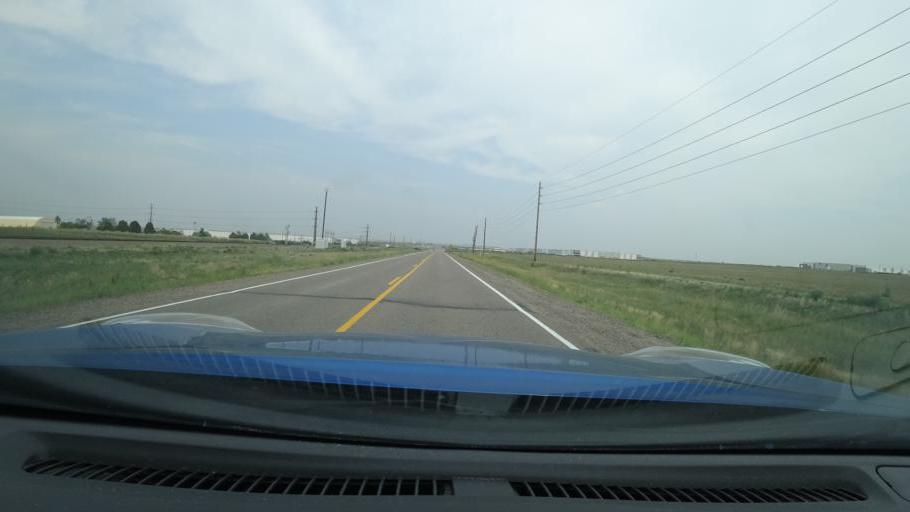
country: US
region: Colorado
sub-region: Adams County
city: Aurora
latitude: 39.7506
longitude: -104.7377
